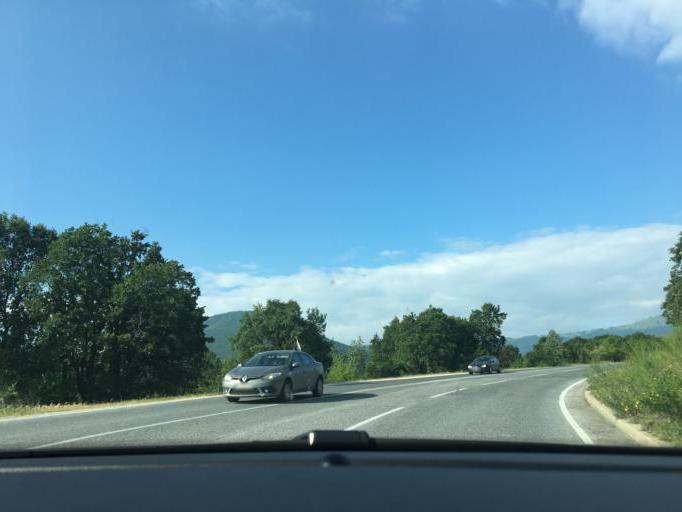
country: MK
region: Prilep
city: Prilep
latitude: 41.3810
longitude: 21.7445
